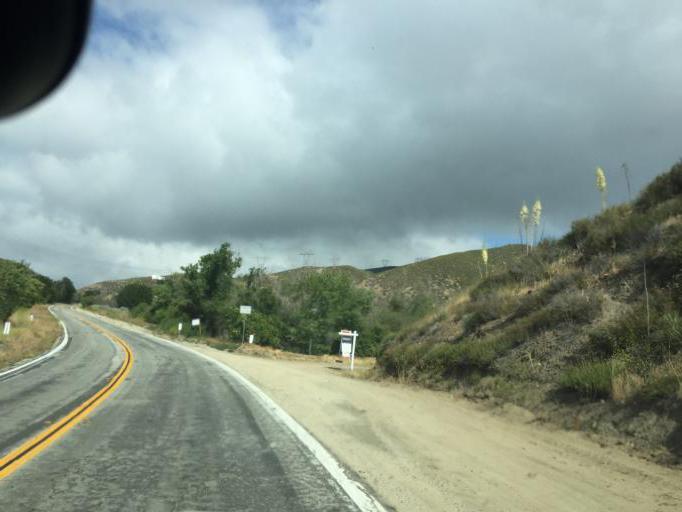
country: US
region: California
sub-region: Los Angeles County
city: Leona Valley
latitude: 34.5876
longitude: -118.2964
